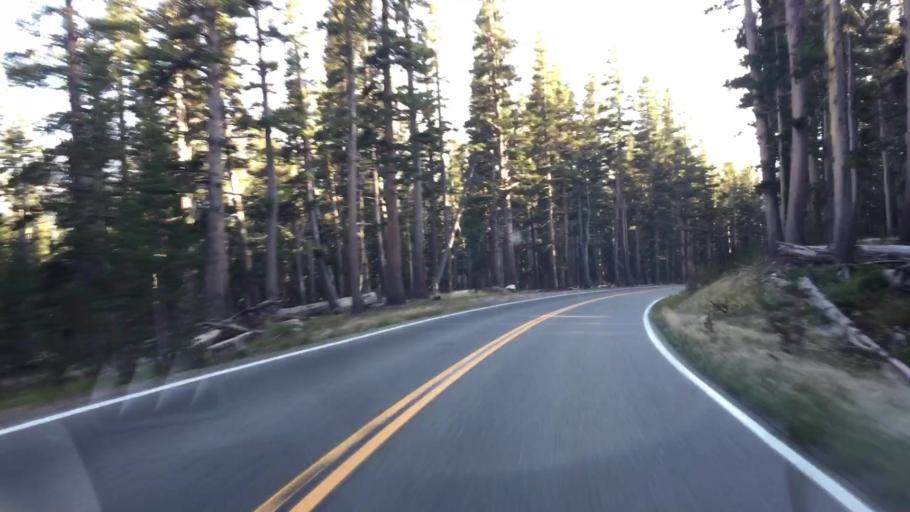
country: US
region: California
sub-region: Mariposa County
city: Yosemite Valley
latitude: 37.8935
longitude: -119.2601
